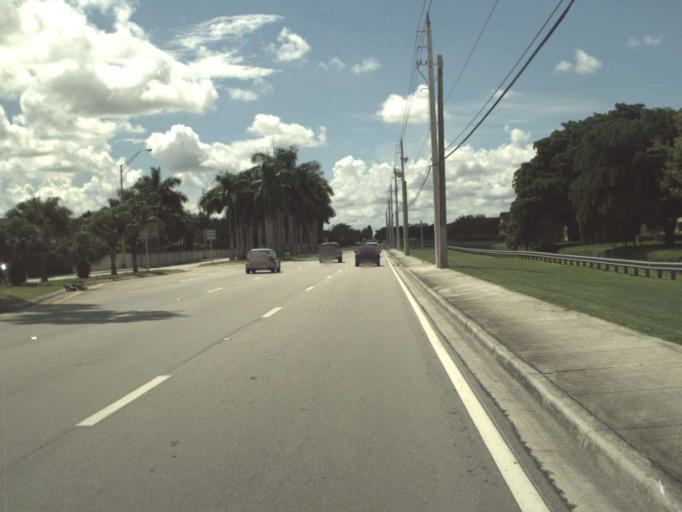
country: US
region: Florida
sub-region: Miami-Dade County
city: The Crossings
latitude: 25.6770
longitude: -80.4167
